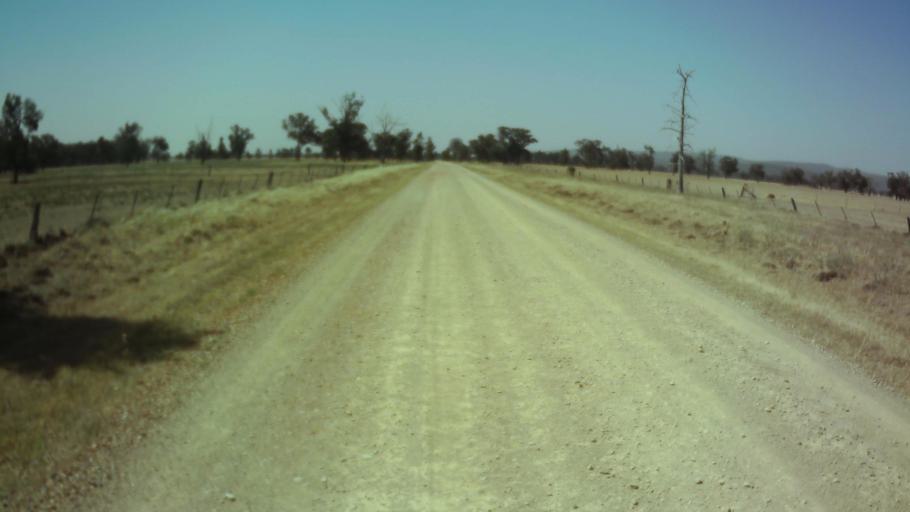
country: AU
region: New South Wales
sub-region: Weddin
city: Grenfell
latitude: -34.0250
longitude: 147.9137
